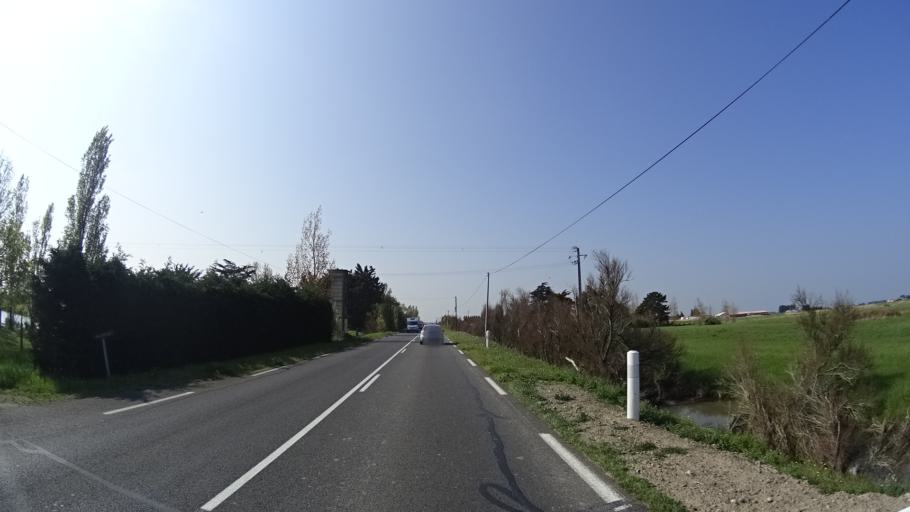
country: FR
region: Pays de la Loire
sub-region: Departement de la Vendee
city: Bouin
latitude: 46.9983
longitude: -1.9663
